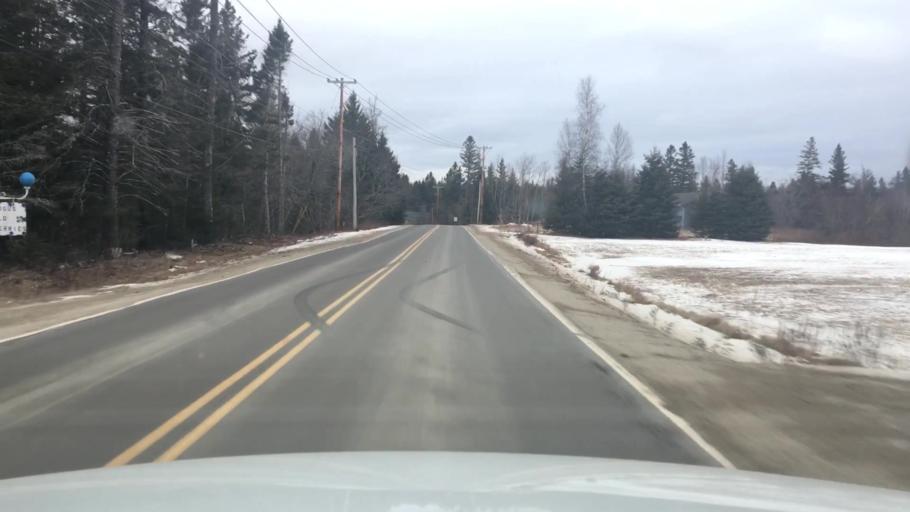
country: US
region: Maine
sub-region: Washington County
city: Addison
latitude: 44.6234
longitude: -67.7117
